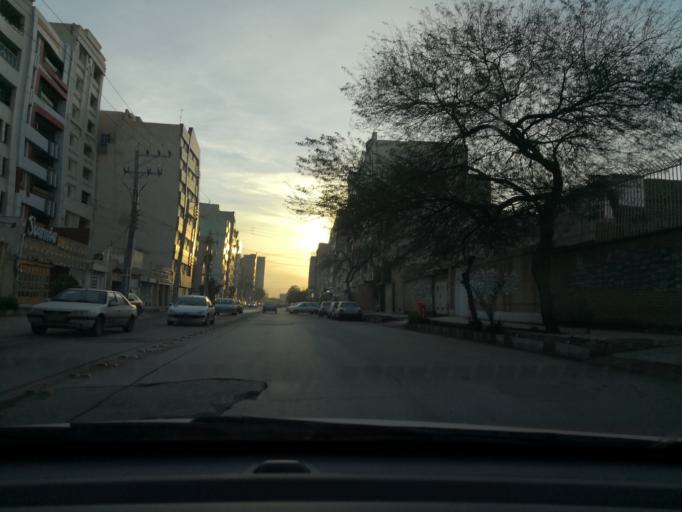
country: IR
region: Khuzestan
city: Ahvaz
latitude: 31.3494
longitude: 48.6900
